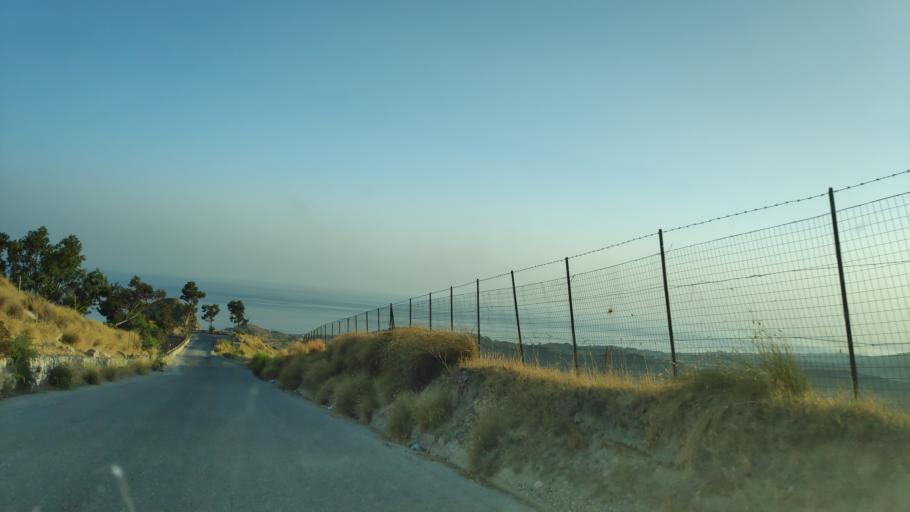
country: IT
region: Calabria
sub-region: Provincia di Reggio Calabria
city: Bova Marina
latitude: 37.9549
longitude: 15.9210
